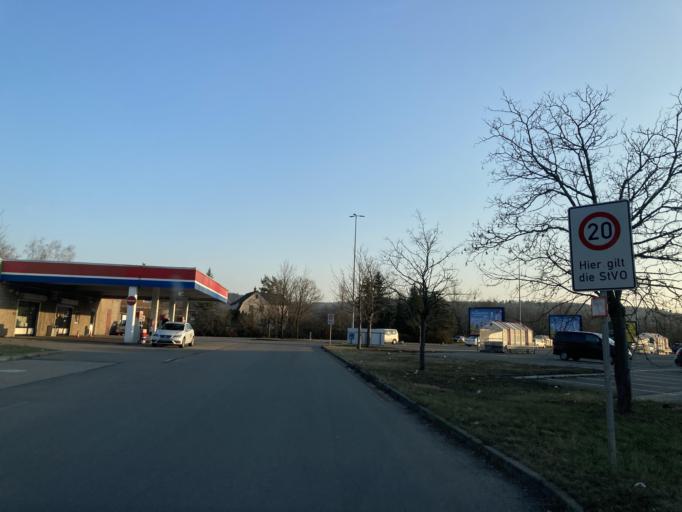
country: DE
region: Baden-Wuerttemberg
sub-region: Tuebingen Region
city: Tuebingen
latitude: 48.4965
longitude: 9.0307
